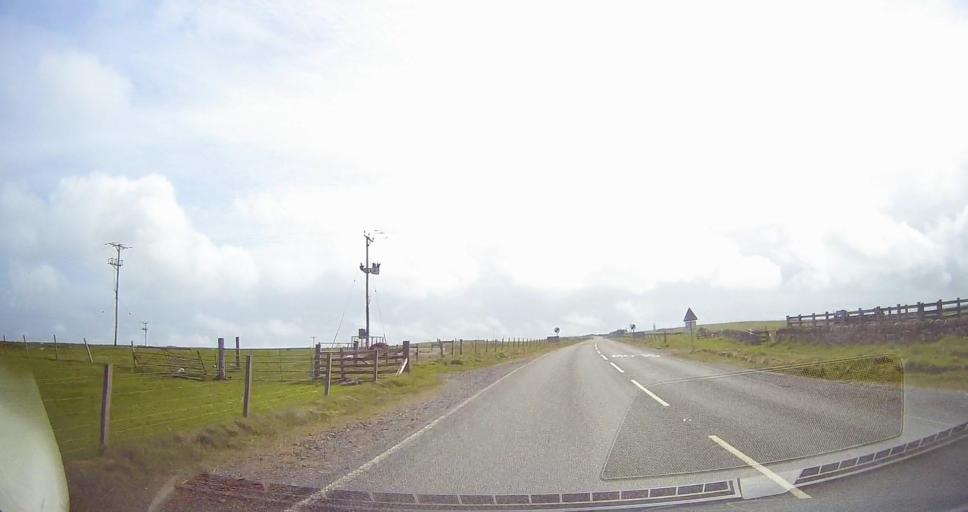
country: GB
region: Scotland
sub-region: Shetland Islands
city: Sandwick
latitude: 59.9191
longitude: -1.2996
